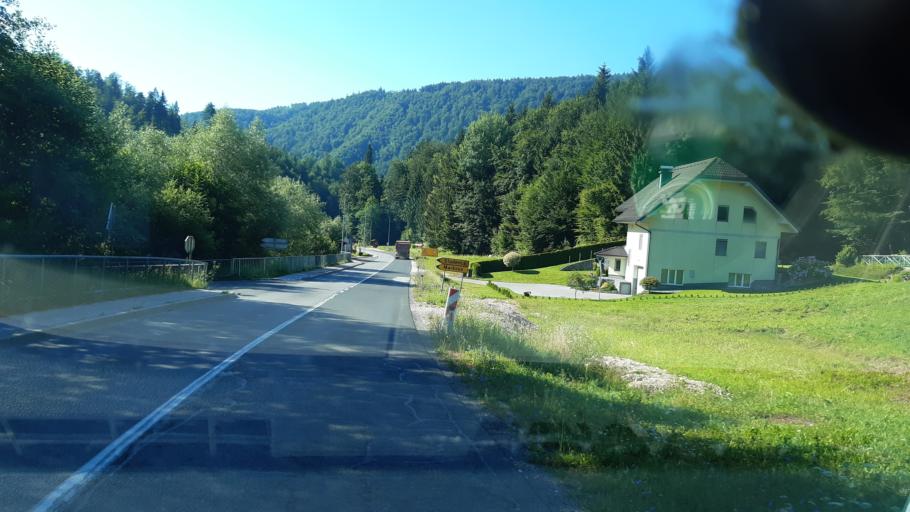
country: SI
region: Kamnik
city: Mekinje
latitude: 46.2340
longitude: 14.6662
